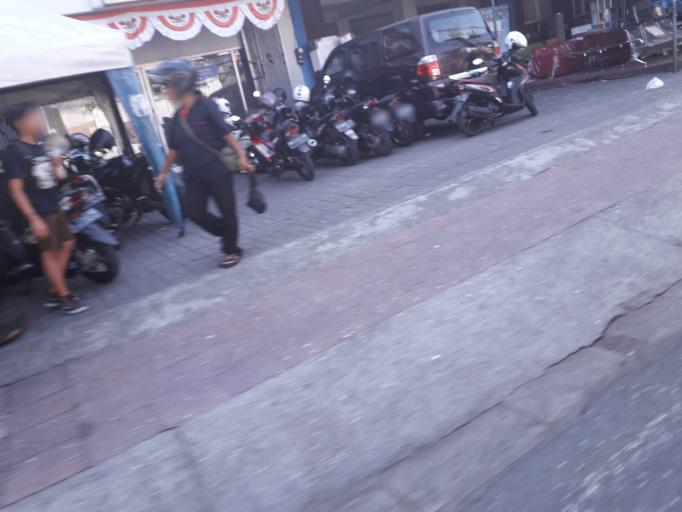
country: ID
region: Daerah Istimewa Yogyakarta
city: Yogyakarta
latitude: -7.7985
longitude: 110.3694
